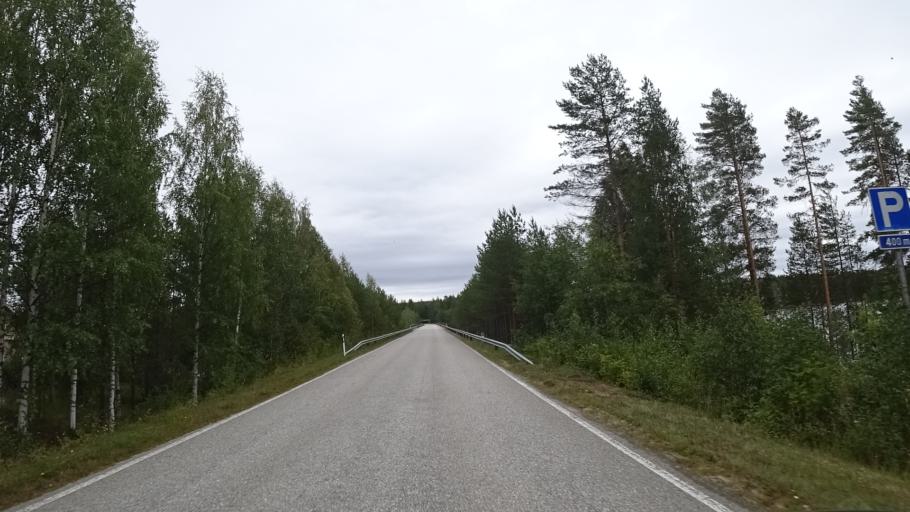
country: FI
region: North Karelia
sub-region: Pielisen Karjala
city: Lieksa
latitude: 63.3839
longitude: 30.3306
